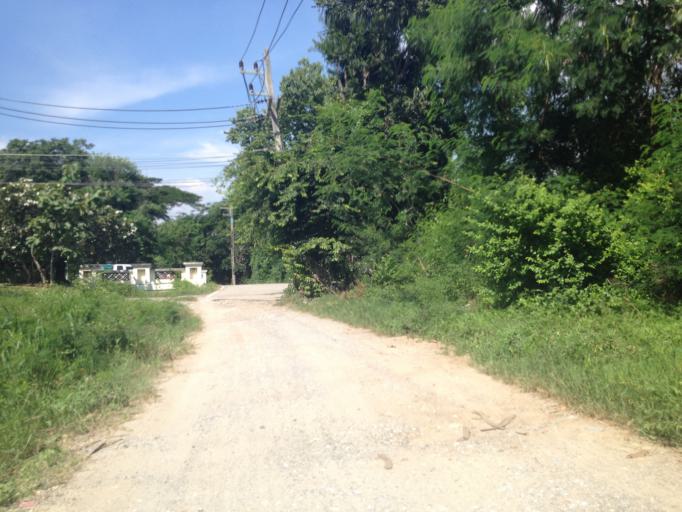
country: TH
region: Chiang Mai
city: Chiang Mai
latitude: 18.7570
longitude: 98.9439
